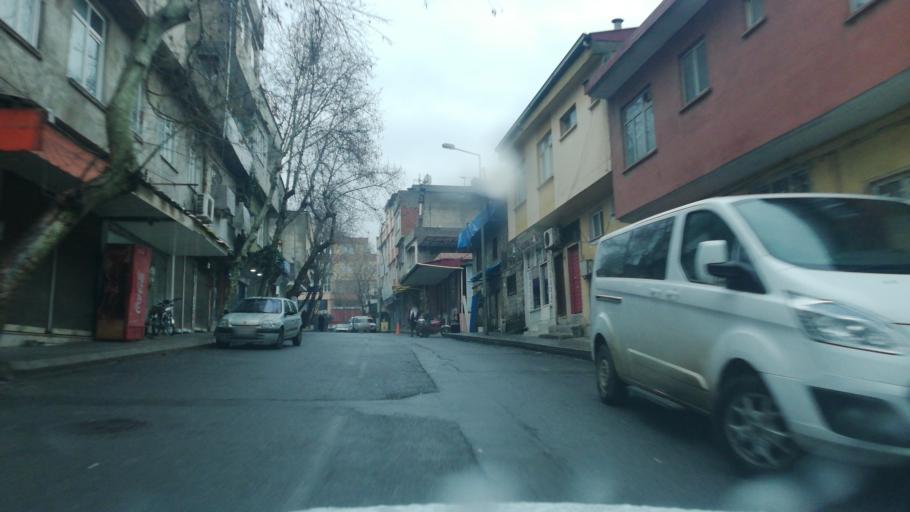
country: TR
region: Kahramanmaras
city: Kahramanmaras
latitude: 37.5813
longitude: 36.9380
